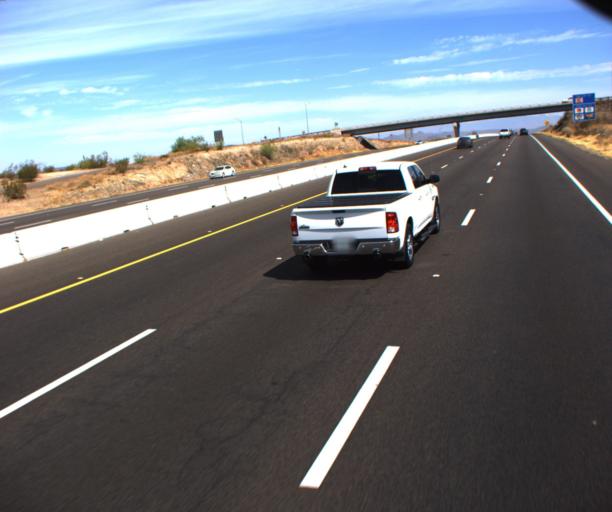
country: US
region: Arizona
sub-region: Maricopa County
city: Anthem
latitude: 33.8184
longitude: -112.1407
